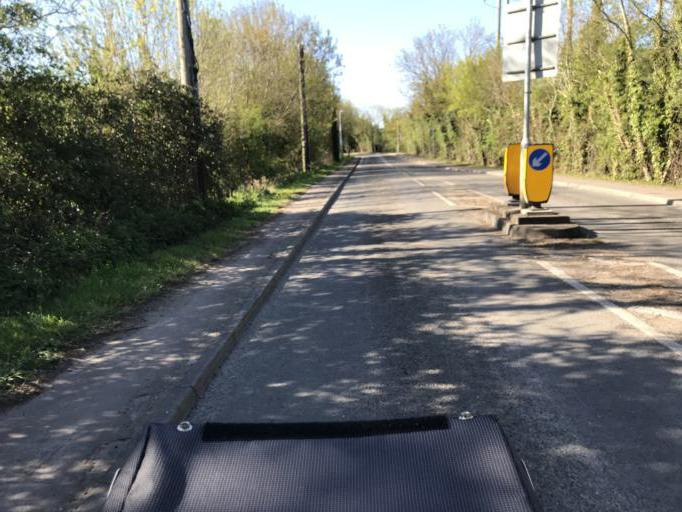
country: GB
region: England
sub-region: Cambridgeshire
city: Fulbourn
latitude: 52.1970
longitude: 0.1982
